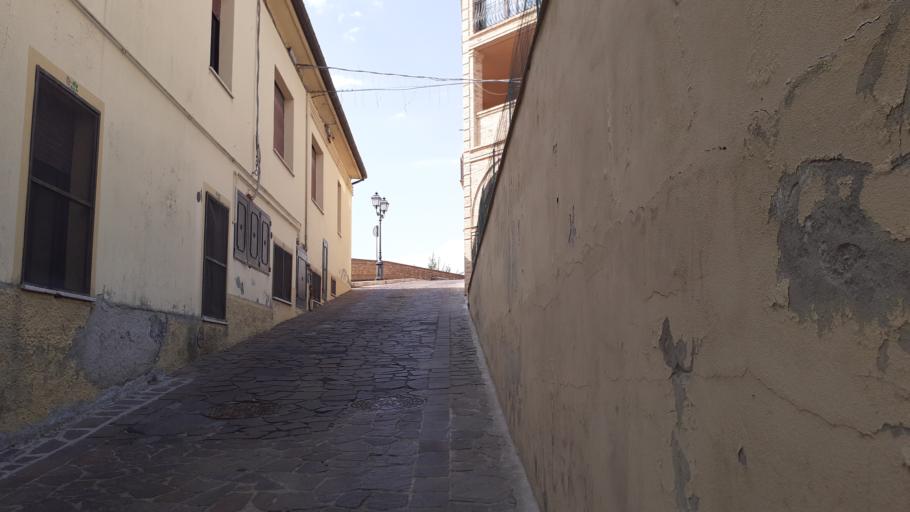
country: IT
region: Abruzzo
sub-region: Provincia di Chieti
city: Vacri
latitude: 42.2975
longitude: 14.2326
